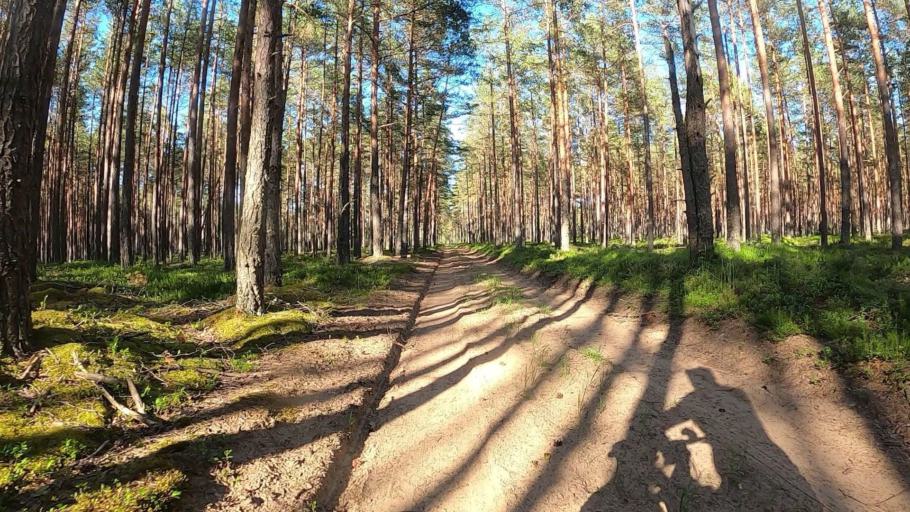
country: LV
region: Carnikava
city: Carnikava
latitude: 57.1097
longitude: 24.2405
